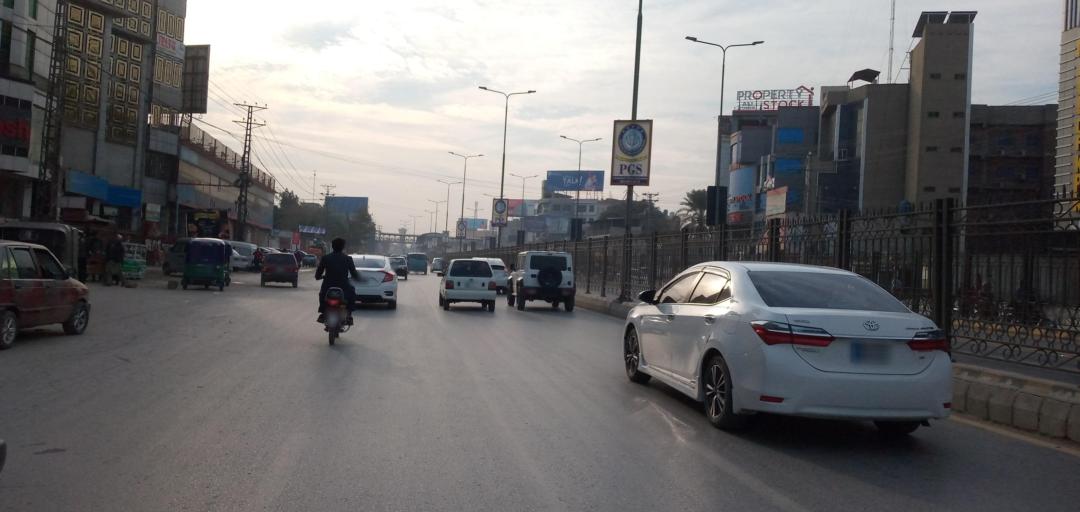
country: PK
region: Khyber Pakhtunkhwa
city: Peshawar
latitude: 34.0009
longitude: 71.4978
